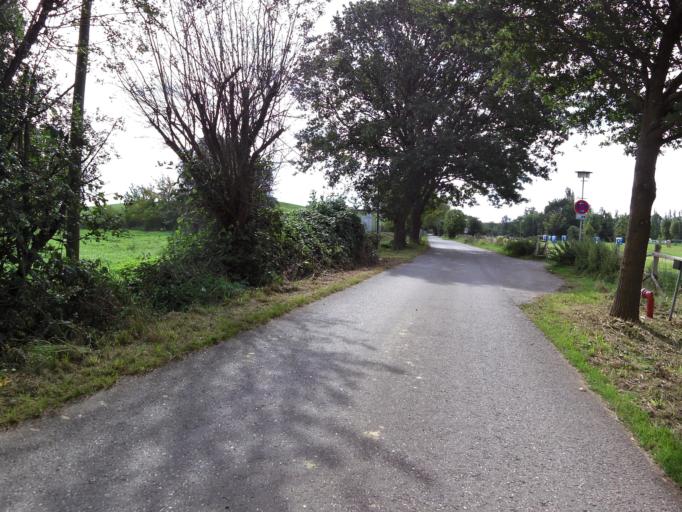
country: DE
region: Saxony-Anhalt
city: Havelberg
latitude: 52.8295
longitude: 12.0569
